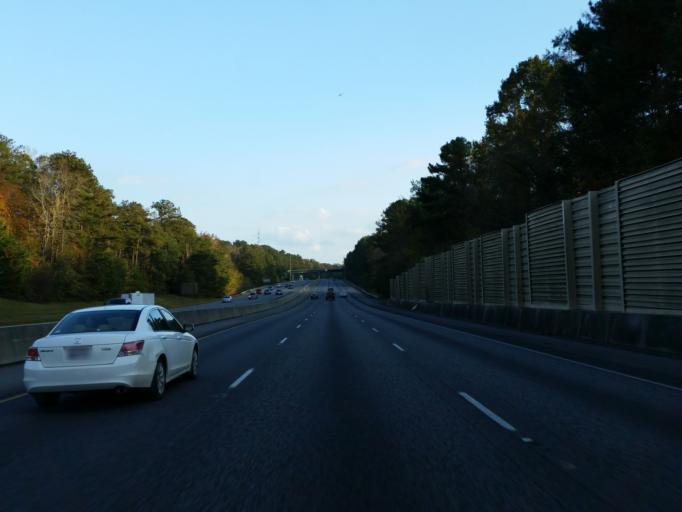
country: US
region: Georgia
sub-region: Bibb County
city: West Point
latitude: 32.8634
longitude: -83.7512
